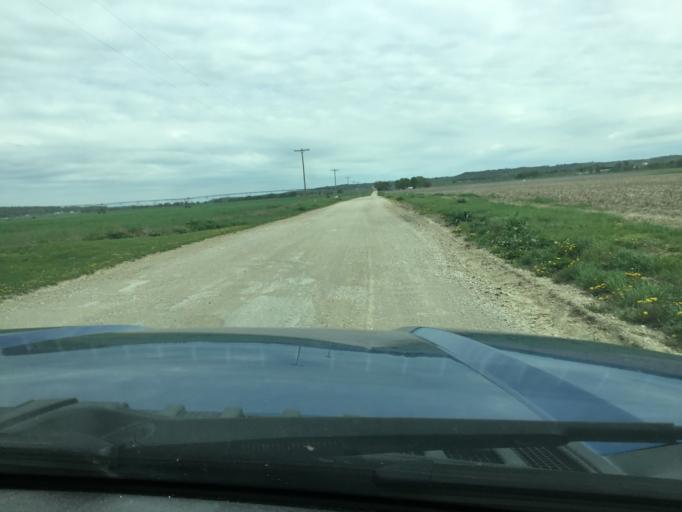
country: US
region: Kansas
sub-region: Douglas County
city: Lawrence
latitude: 39.0103
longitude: -95.2241
